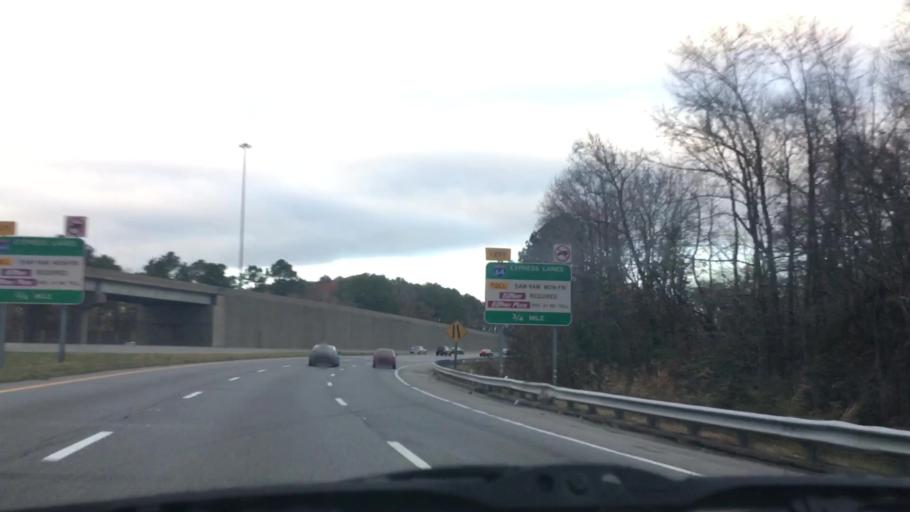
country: US
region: Virginia
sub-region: City of Chesapeake
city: Chesapeake
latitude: 36.8481
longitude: -76.1954
